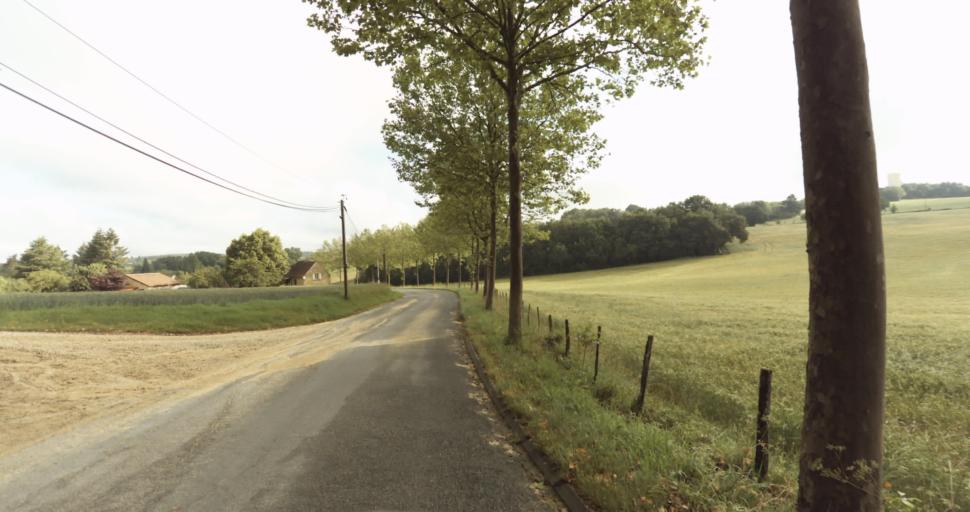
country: FR
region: Aquitaine
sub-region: Departement de la Dordogne
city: Le Bugue
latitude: 44.9426
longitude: 0.8146
